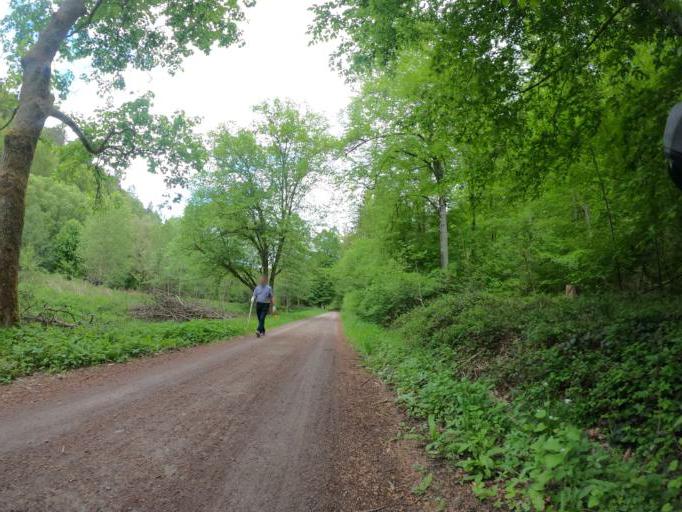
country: DE
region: Baden-Wuerttemberg
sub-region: Tuebingen Region
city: Dettenhausen
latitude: 48.6001
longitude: 9.1261
